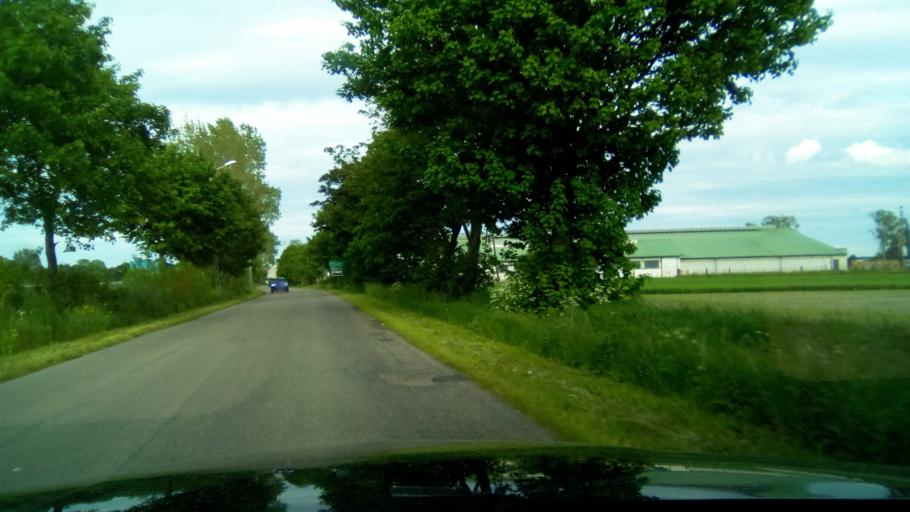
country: PL
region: Pomeranian Voivodeship
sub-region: Powiat pucki
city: Krokowa
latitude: 54.8084
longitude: 18.1839
